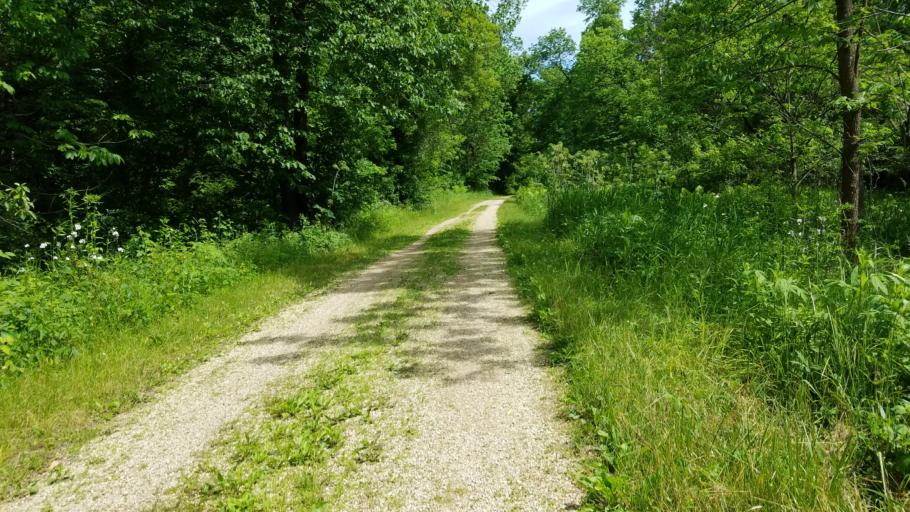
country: US
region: Wisconsin
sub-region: Dunn County
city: Menomonie
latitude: 44.8192
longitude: -91.9486
